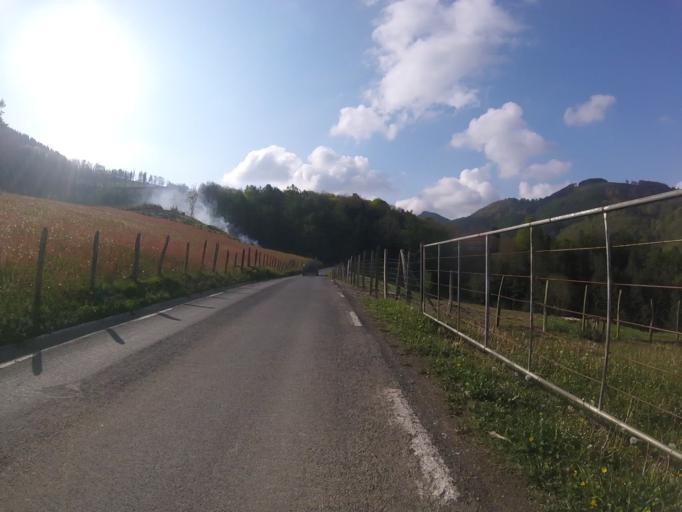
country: ES
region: Basque Country
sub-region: Provincia de Guipuzcoa
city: Azkoitia
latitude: 43.2279
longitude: -2.3190
